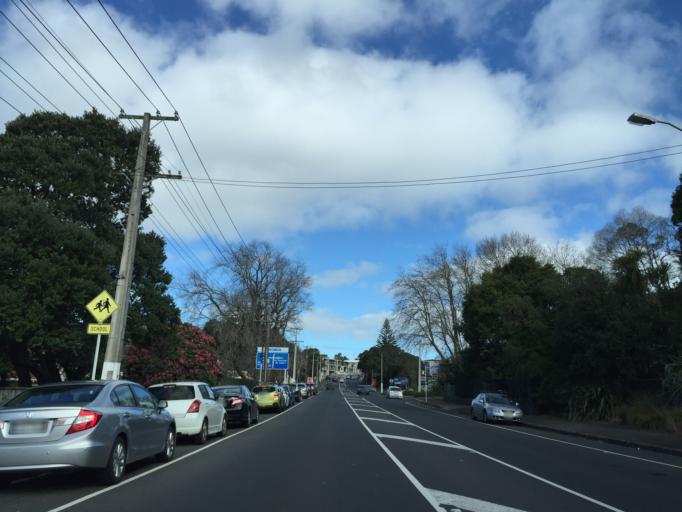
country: NZ
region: Auckland
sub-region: Auckland
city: Auckland
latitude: -36.9066
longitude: 174.7590
